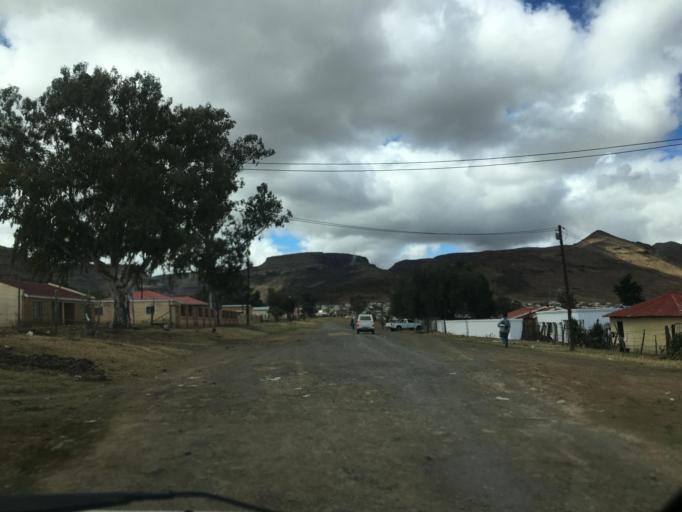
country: ZA
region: Eastern Cape
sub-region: Chris Hani District Municipality
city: Cala
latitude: -31.5281
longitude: 27.6987
